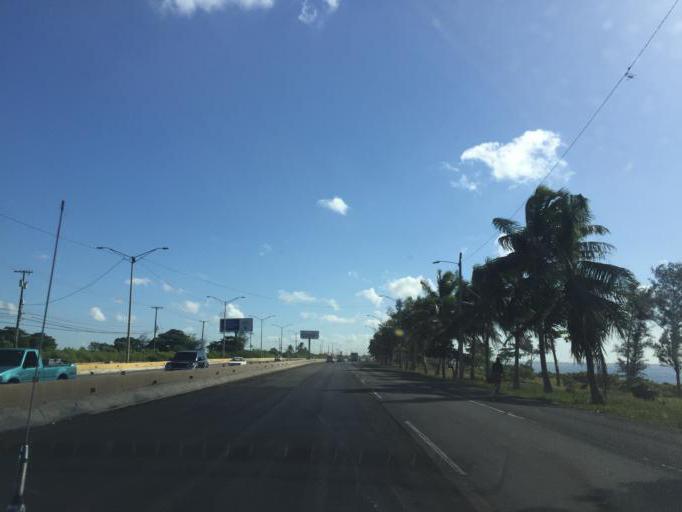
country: DO
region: Santo Domingo
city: Guerra
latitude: 18.4636
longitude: -69.7471
